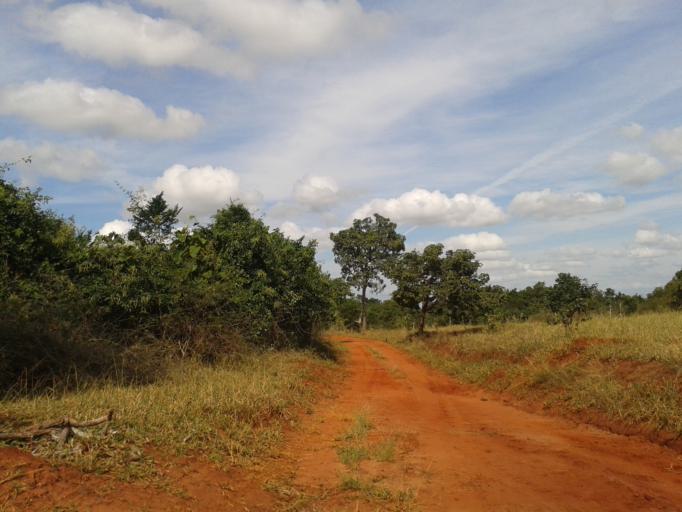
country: BR
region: Minas Gerais
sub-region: Campina Verde
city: Campina Verde
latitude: -19.4450
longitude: -49.6615
